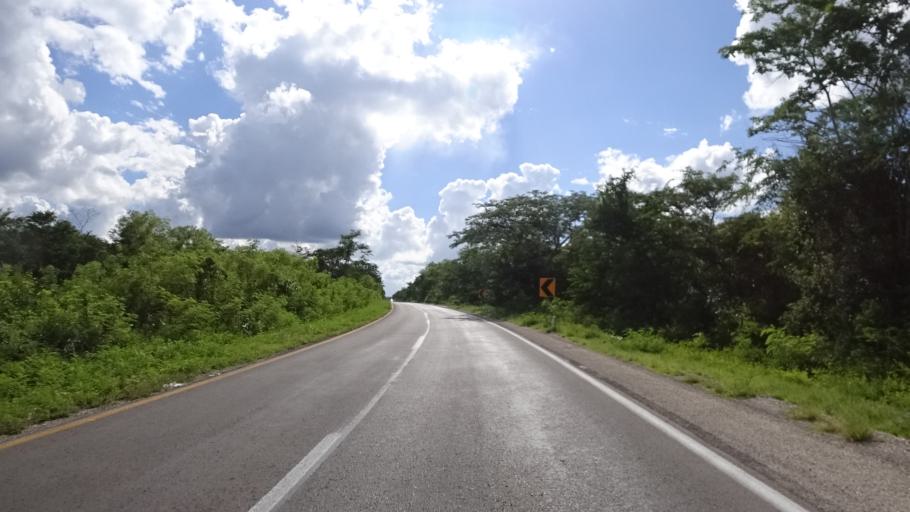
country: MX
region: Yucatan
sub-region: Kantunil
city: Kantunil
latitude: 20.8081
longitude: -89.0355
